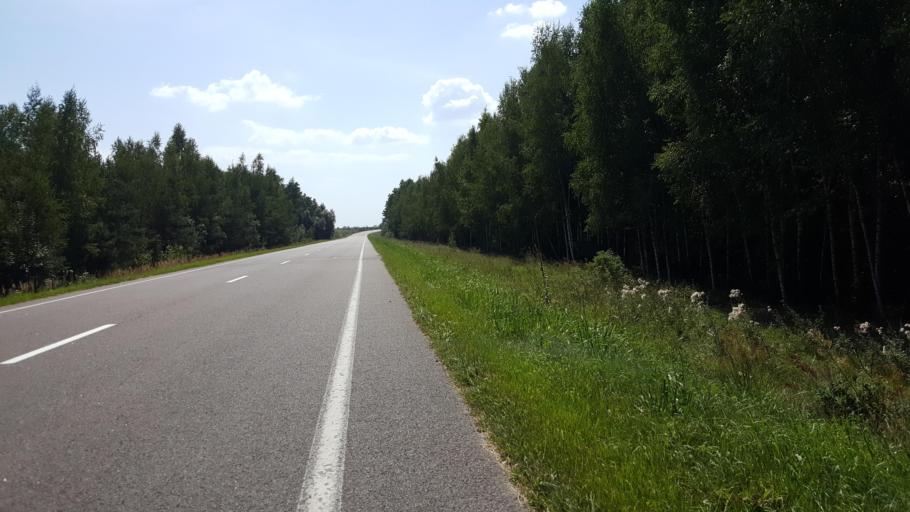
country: PL
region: Podlasie
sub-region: Powiat hajnowski
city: Czeremcha
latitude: 52.5192
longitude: 23.5345
